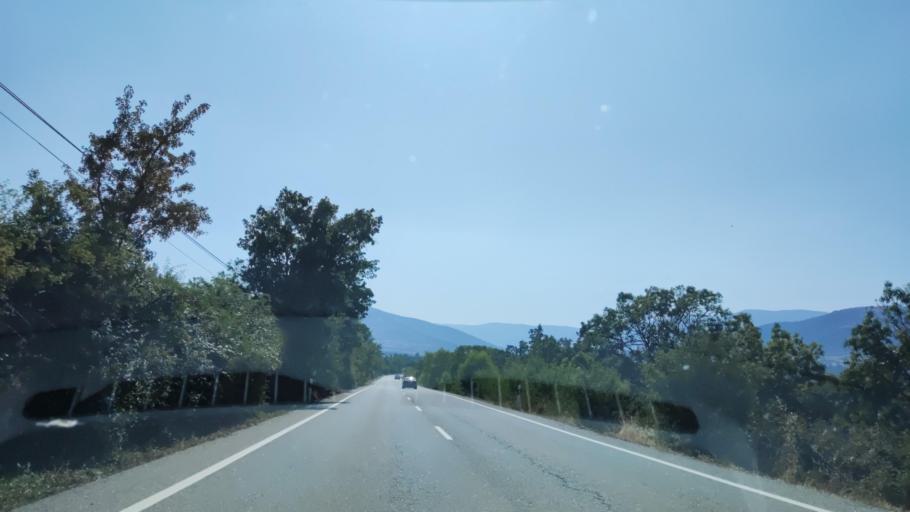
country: ES
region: Madrid
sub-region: Provincia de Madrid
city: Garganta de los Montes
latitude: 40.9441
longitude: -3.6793
